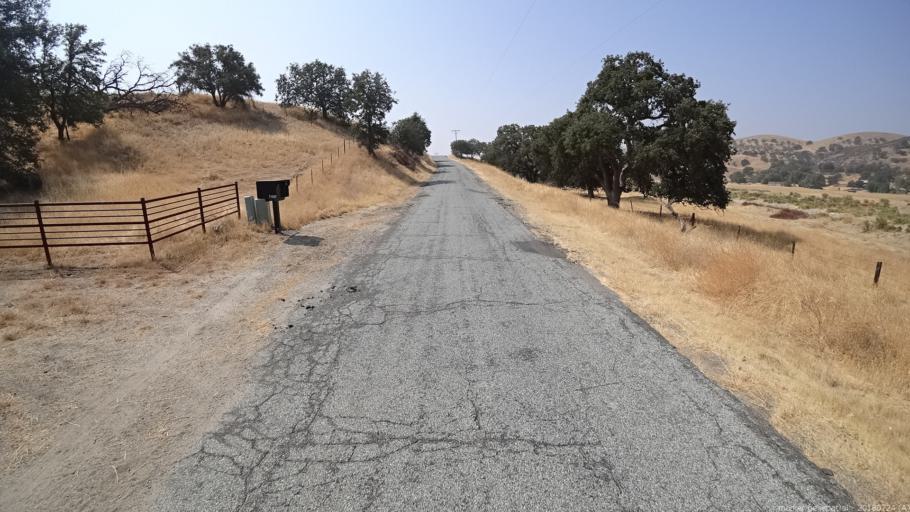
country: US
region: California
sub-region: San Luis Obispo County
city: San Miguel
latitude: 35.8920
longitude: -120.7001
